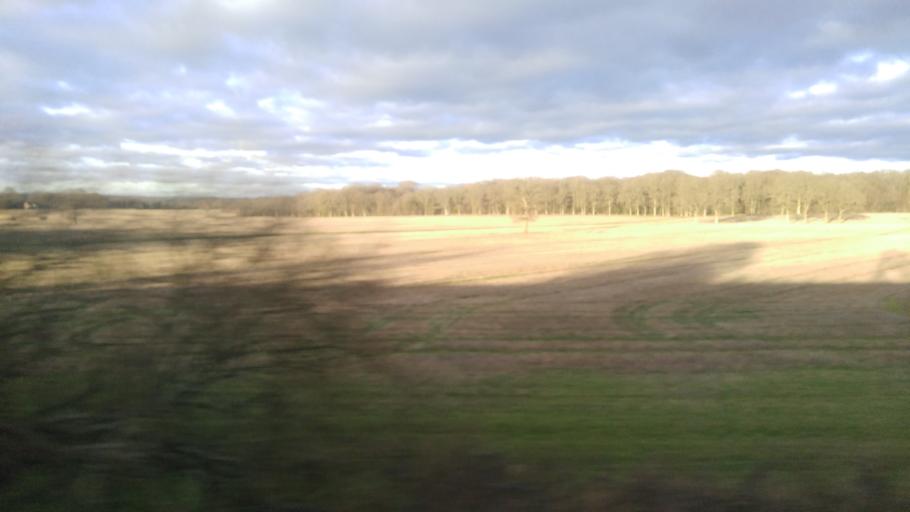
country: GB
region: England
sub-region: Kent
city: Lenham
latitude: 51.1597
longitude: 0.7058
